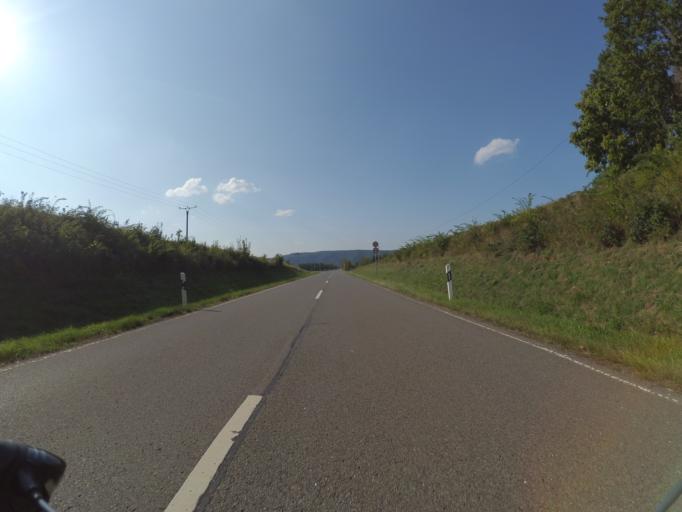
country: DE
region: Rheinland-Pfalz
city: Minheim
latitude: 49.8593
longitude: 6.9296
